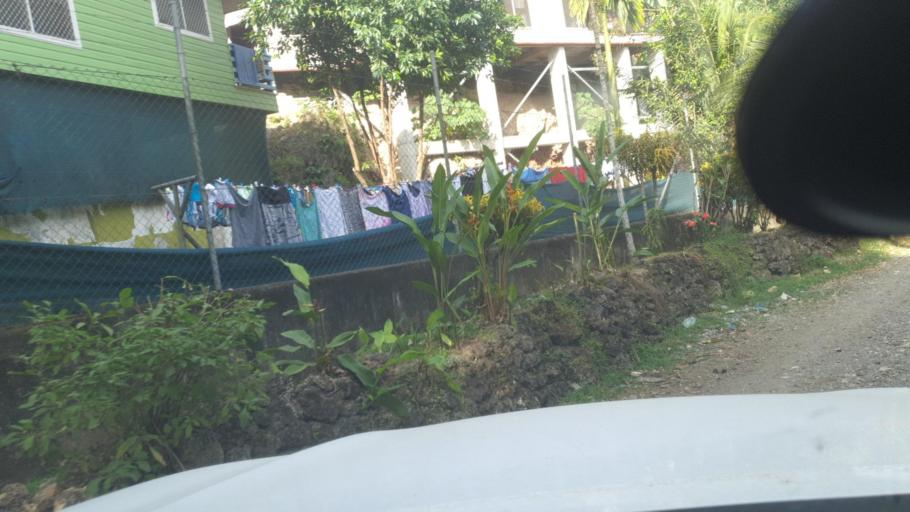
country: SB
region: Guadalcanal
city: Honiara
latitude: -9.4378
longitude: 159.9446
